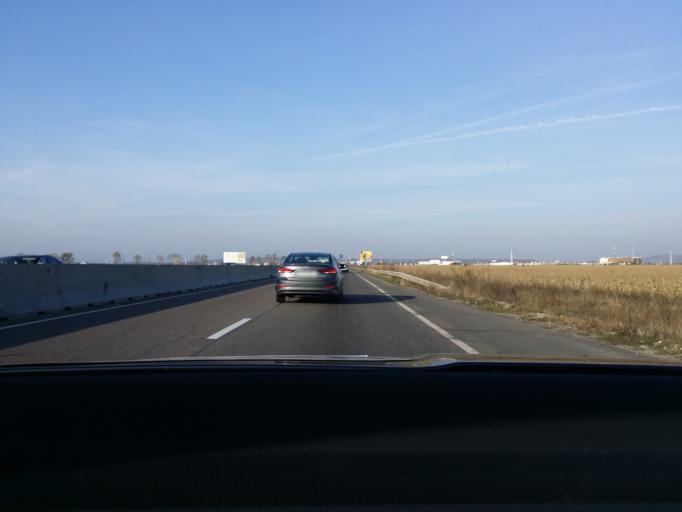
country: RO
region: Prahova
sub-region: Comuna Targsoru Vechi
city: Strejnicu
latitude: 44.9515
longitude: 25.9627
